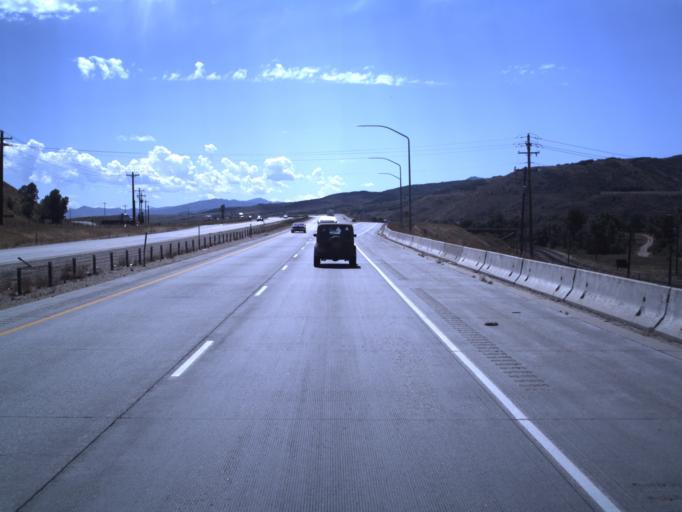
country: US
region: Utah
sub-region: Morgan County
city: Mountain Green
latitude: 41.1202
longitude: -111.7647
